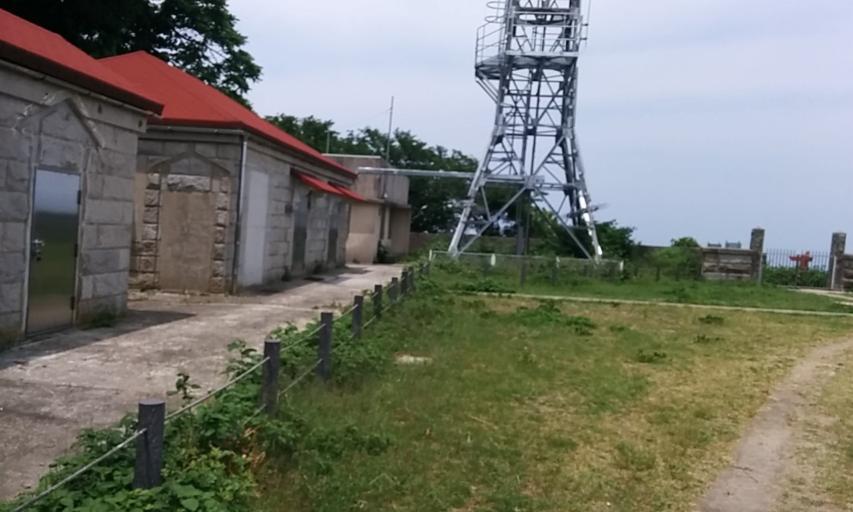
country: JP
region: Kyoto
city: Miyazu
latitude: 35.7768
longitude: 135.2233
